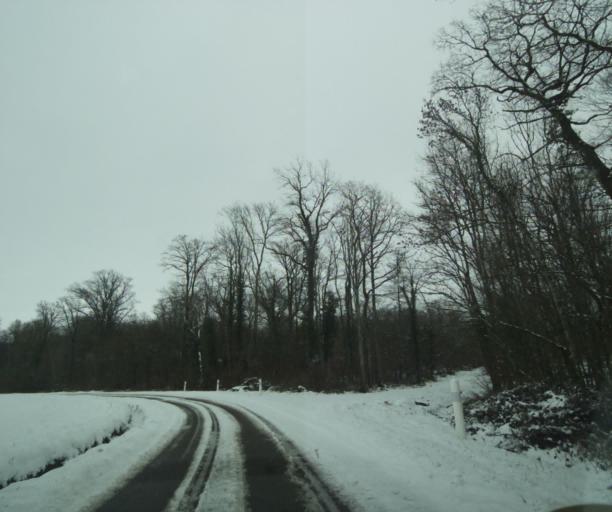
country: FR
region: Champagne-Ardenne
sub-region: Departement de la Haute-Marne
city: Montier-en-Der
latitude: 48.4160
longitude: 4.7556
